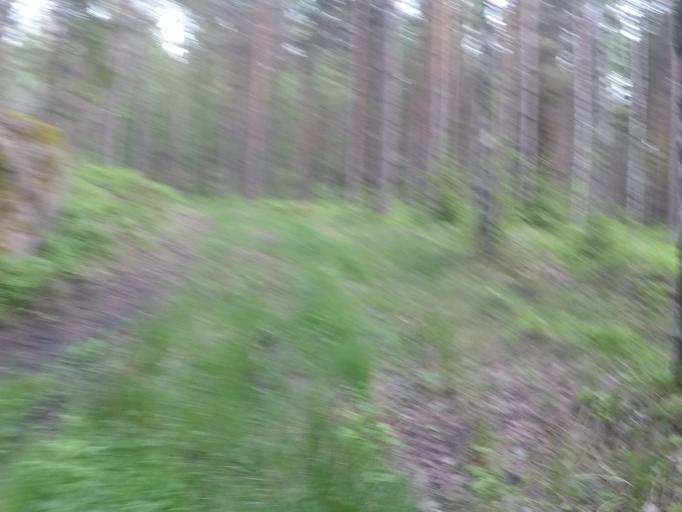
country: SE
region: Soedermanland
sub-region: Eskilstuna Kommun
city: Kvicksund
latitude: 59.4068
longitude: 16.3177
